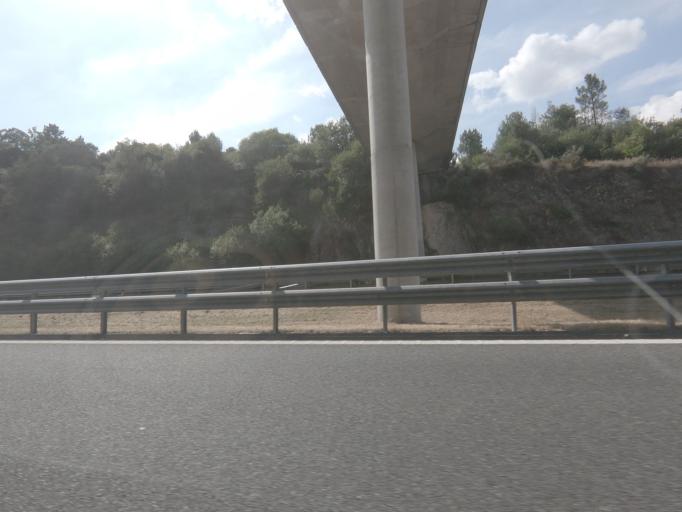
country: ES
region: Galicia
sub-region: Provincia de Ourense
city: Cenlle
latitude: 42.3307
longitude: -8.0744
